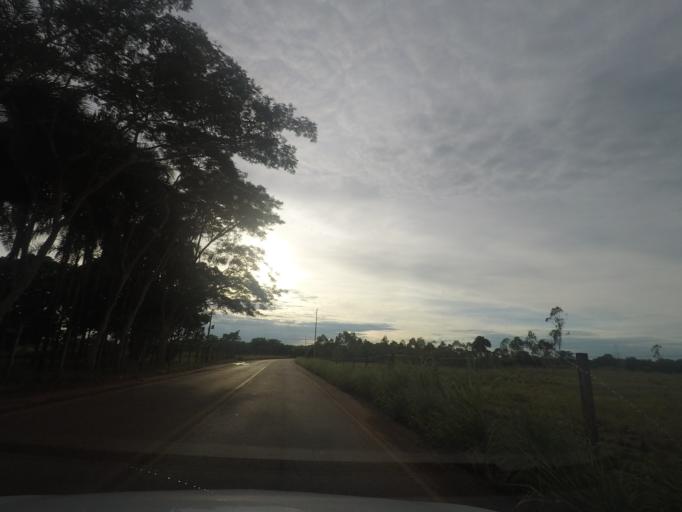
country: BR
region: Goias
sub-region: Trindade
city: Trindade
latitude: -16.7340
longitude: -49.4189
